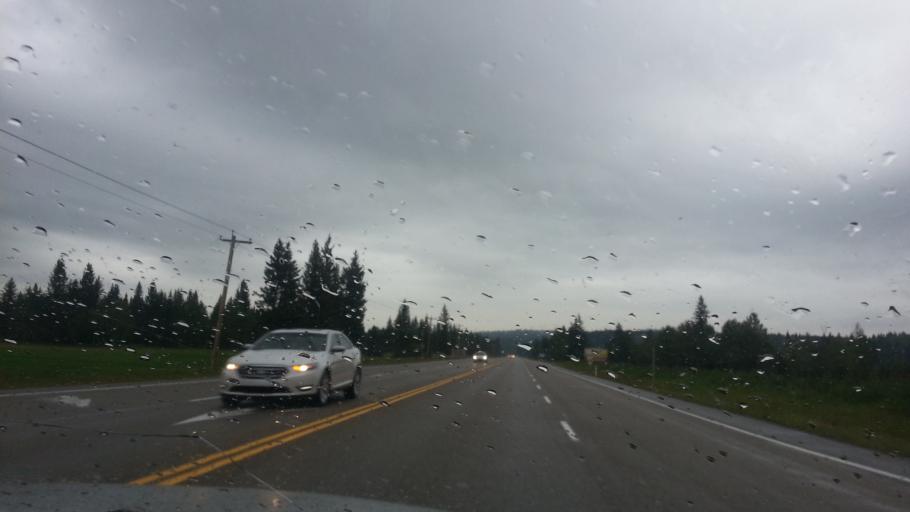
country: CA
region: Alberta
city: Cochrane
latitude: 50.9770
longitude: -114.5218
